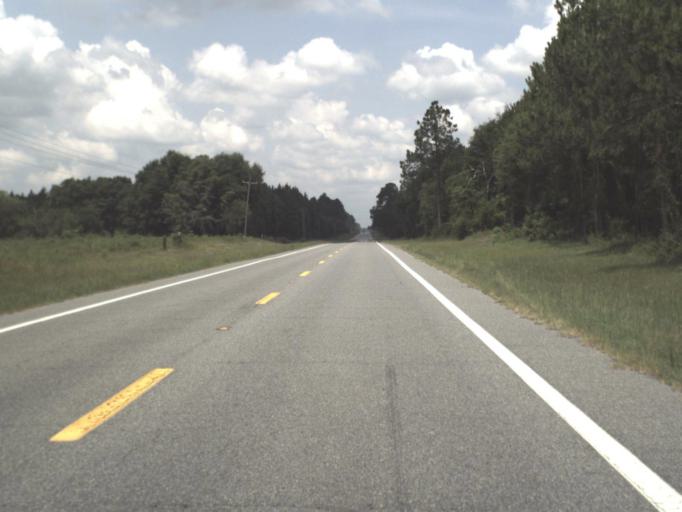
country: US
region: Florida
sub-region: Hamilton County
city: Jasper
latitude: 30.4902
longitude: -83.1163
